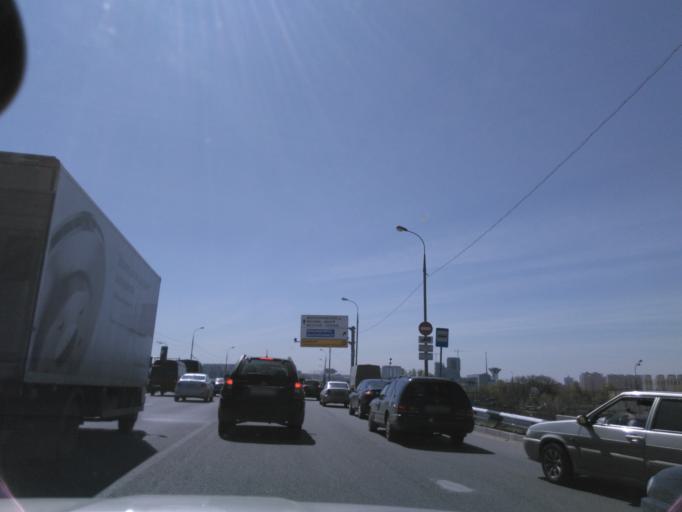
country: RU
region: Moscow
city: Strogino
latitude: 55.8349
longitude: 37.3959
